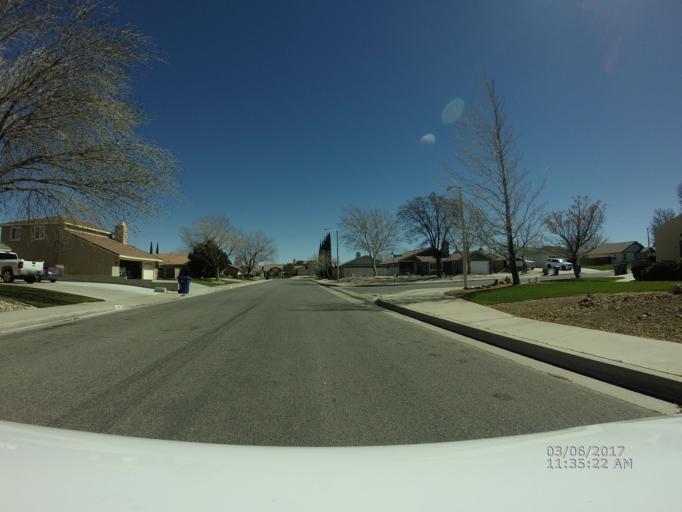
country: US
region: California
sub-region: Los Angeles County
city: Quartz Hill
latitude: 34.6523
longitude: -118.2396
